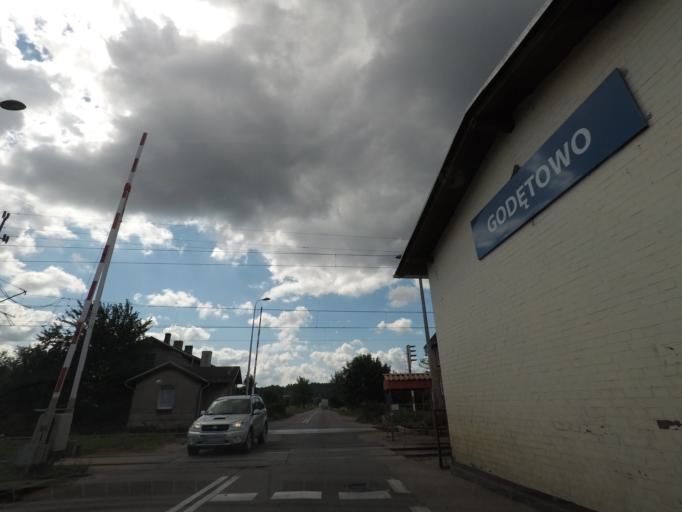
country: PL
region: Pomeranian Voivodeship
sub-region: Powiat wejherowski
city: Leczyce
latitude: 54.5822
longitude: 17.8650
